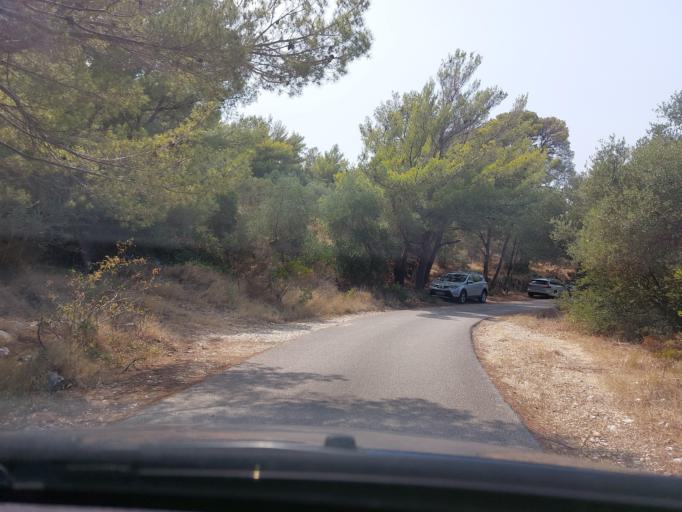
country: HR
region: Dubrovacko-Neretvanska
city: Smokvica
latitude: 42.7266
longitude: 16.8855
